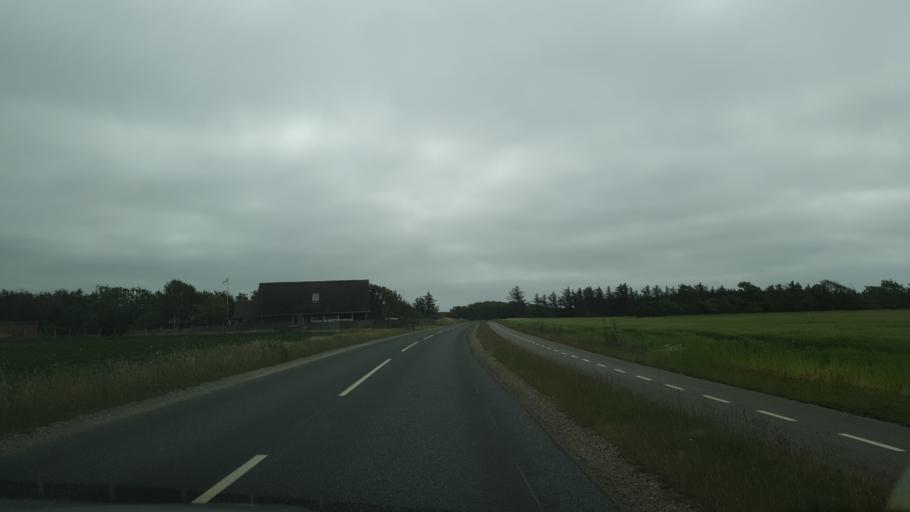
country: DK
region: Central Jutland
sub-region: Ringkobing-Skjern Kommune
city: Skjern
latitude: 55.9767
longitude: 8.3540
